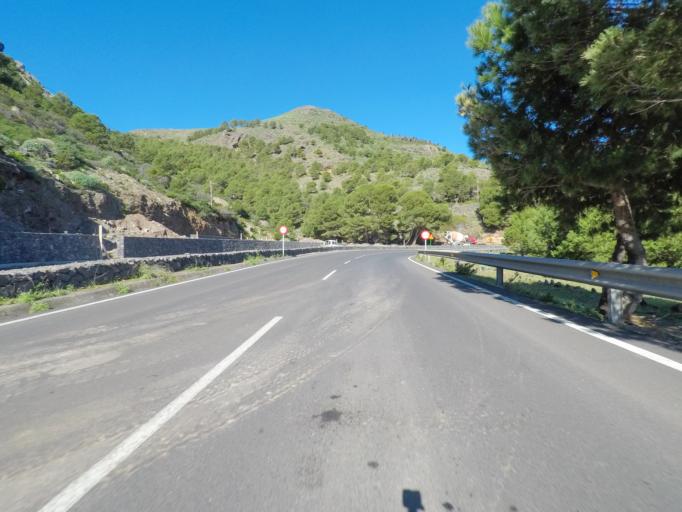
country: ES
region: Canary Islands
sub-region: Provincia de Santa Cruz de Tenerife
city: Alajero
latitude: 28.0836
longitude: -17.1998
